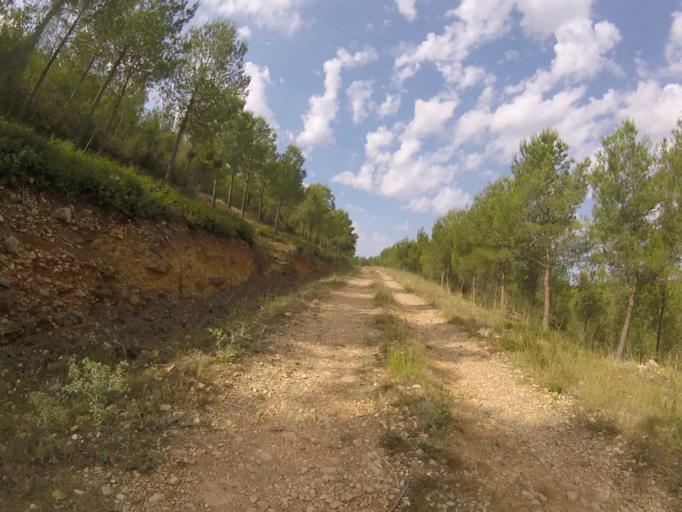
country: ES
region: Valencia
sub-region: Provincia de Castello
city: Alcala de Xivert
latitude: 40.3651
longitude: 0.2037
